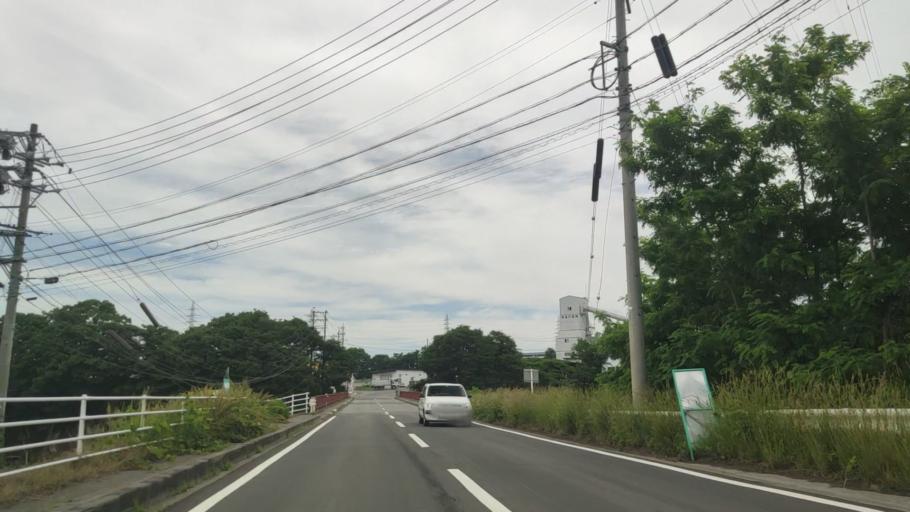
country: JP
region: Nagano
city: Kamimaruko
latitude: 36.3405
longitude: 138.3527
